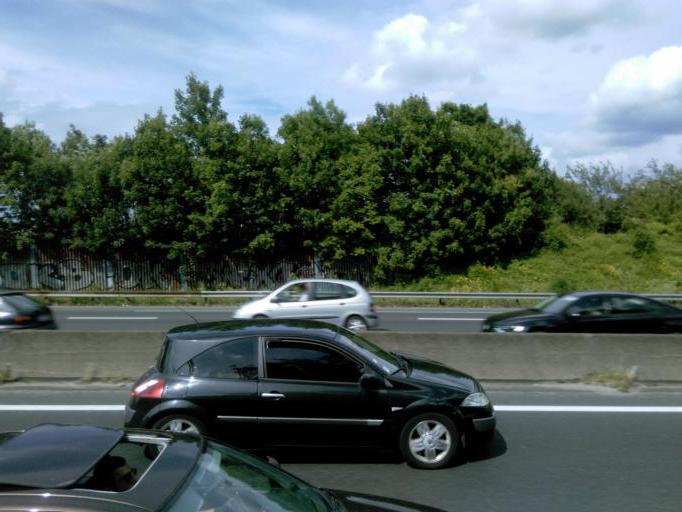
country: FR
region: Ile-de-France
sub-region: Departement du Val-d'Oise
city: Franconville
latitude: 48.9799
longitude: 2.2266
